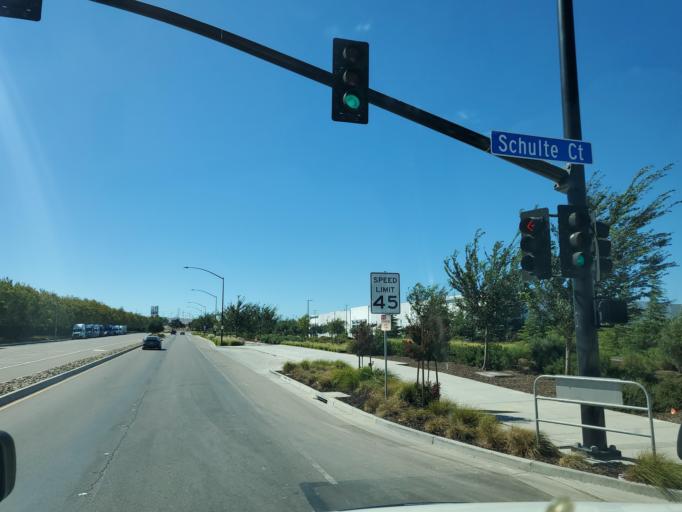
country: US
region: California
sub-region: San Joaquin County
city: Mountain House
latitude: 37.7221
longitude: -121.5267
